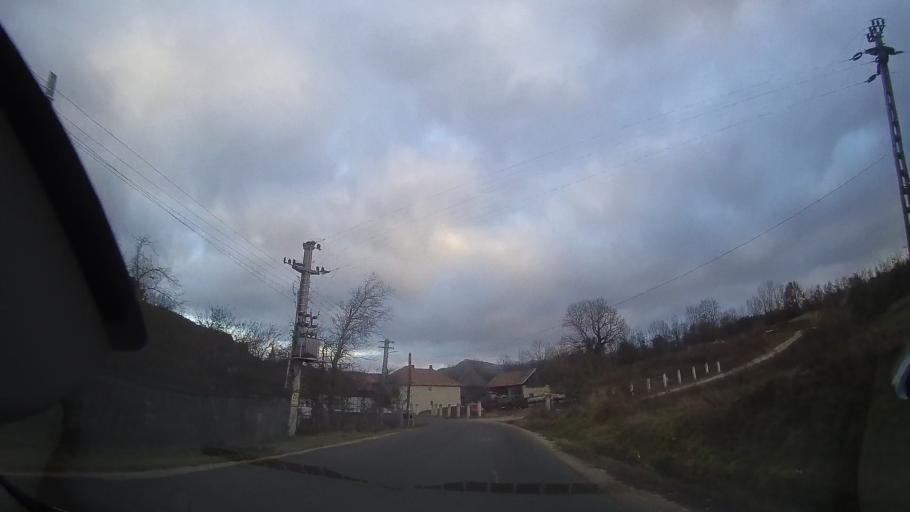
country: RO
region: Cluj
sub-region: Comuna Calatele
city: Calatele
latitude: 46.7820
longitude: 23.0232
